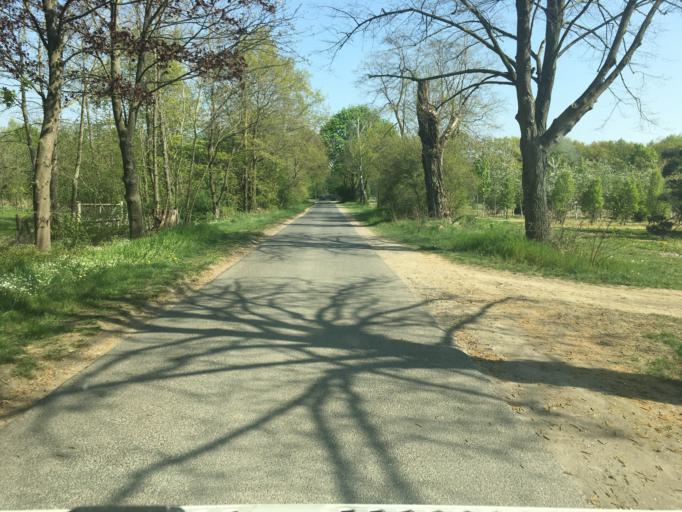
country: DE
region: North Rhine-Westphalia
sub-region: Regierungsbezirk Koln
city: Frechen
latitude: 50.9336
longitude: 6.7423
